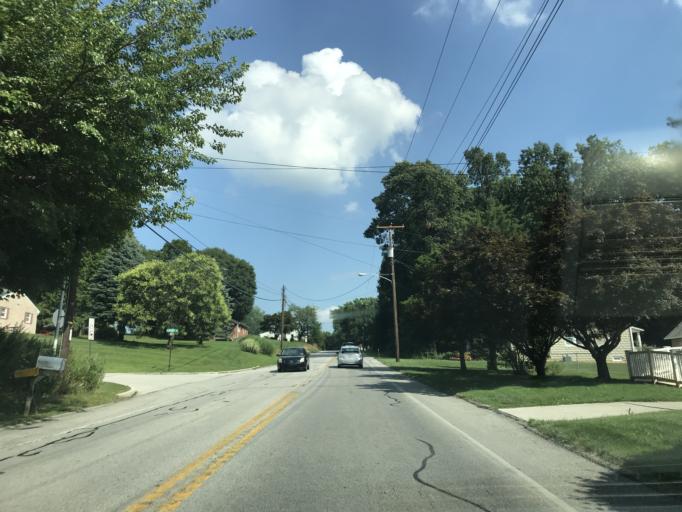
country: US
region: Pennsylvania
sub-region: York County
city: Parkville
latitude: 39.7966
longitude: -76.9484
